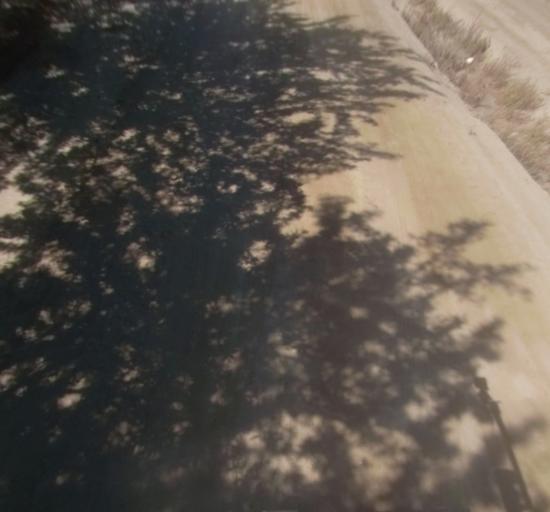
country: US
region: California
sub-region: Fresno County
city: Firebaugh
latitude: 37.0307
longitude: -120.4149
